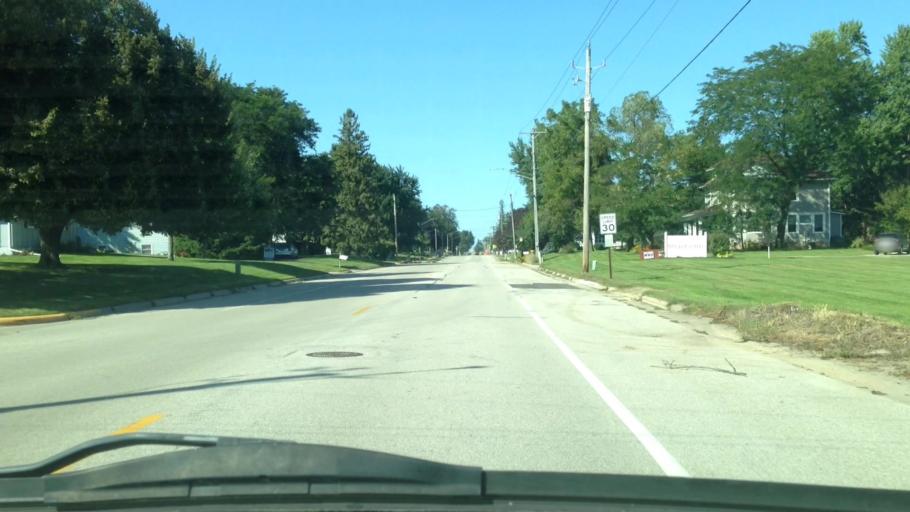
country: US
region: Minnesota
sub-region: Winona County
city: Lewiston
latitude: 43.9773
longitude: -91.8692
